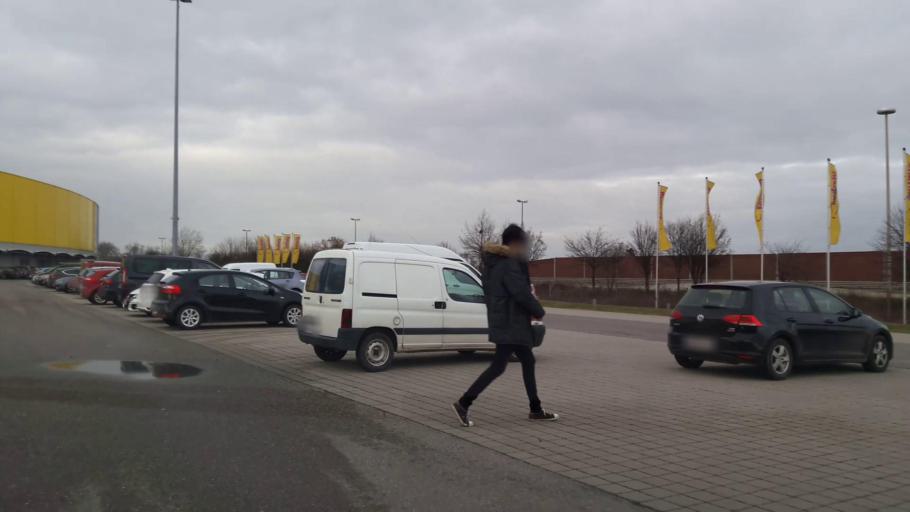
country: AT
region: Lower Austria
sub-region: Politischer Bezirk Wien-Umgebung
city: Gerasdorf bei Wien
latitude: 48.2684
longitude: 16.4761
